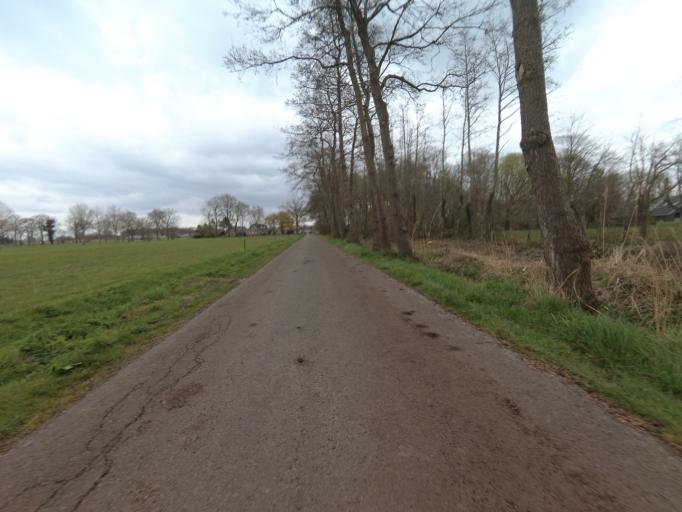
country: NL
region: Gelderland
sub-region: Gemeente Barneveld
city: Terschuur
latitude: 52.1559
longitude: 5.4951
